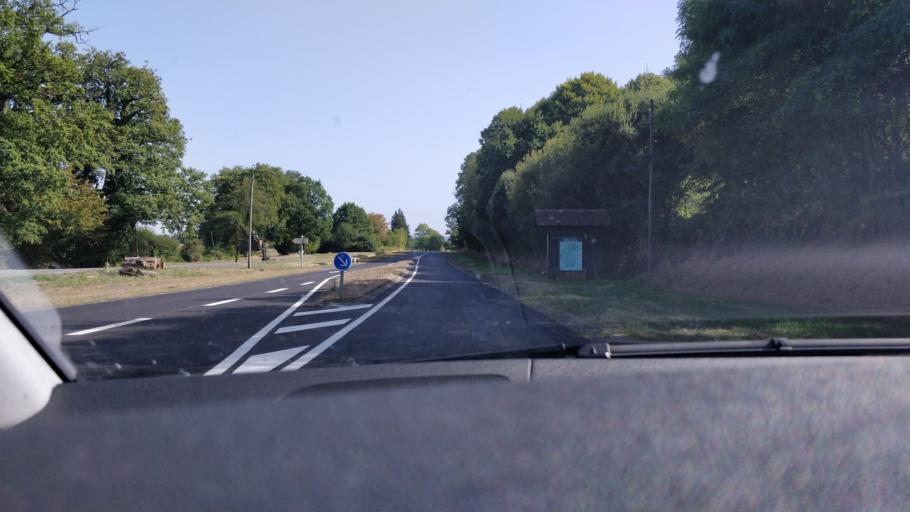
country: FR
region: Limousin
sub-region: Departement de la Correze
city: Uzerche
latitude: 45.4788
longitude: 1.5316
